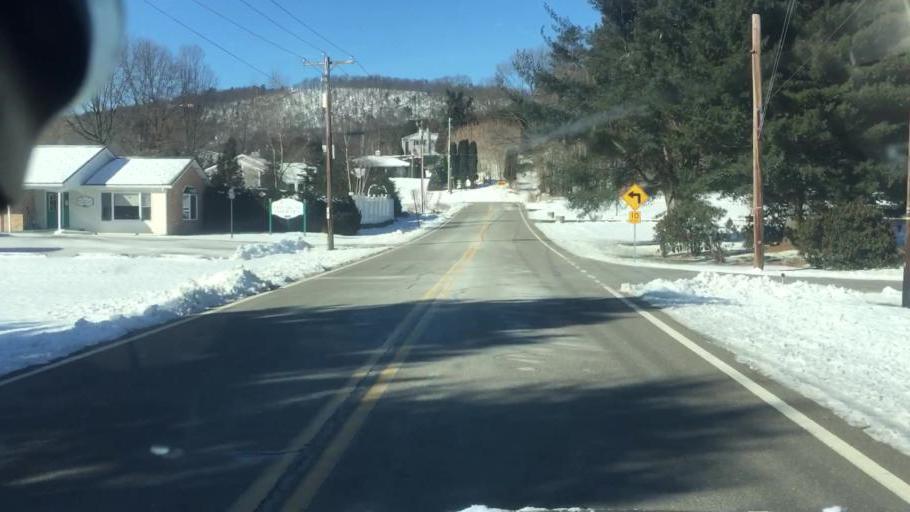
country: US
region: Pennsylvania
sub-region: Luzerne County
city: East Berwick
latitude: 41.0712
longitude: -76.2348
